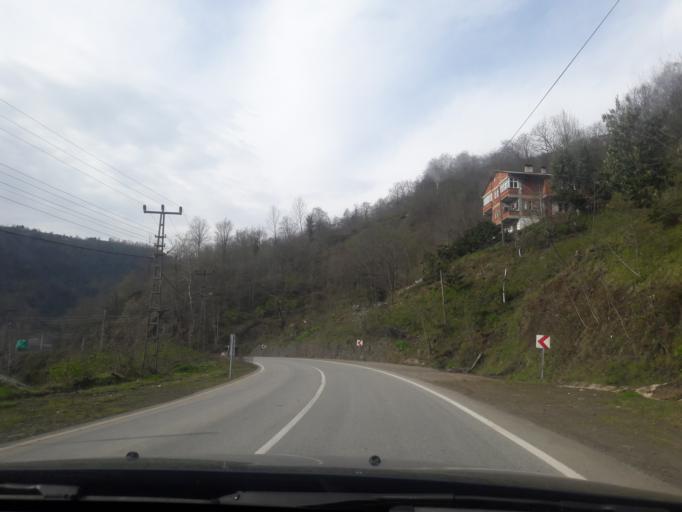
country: TR
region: Trabzon
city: Besikduzu
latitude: 41.0517
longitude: 39.2060
